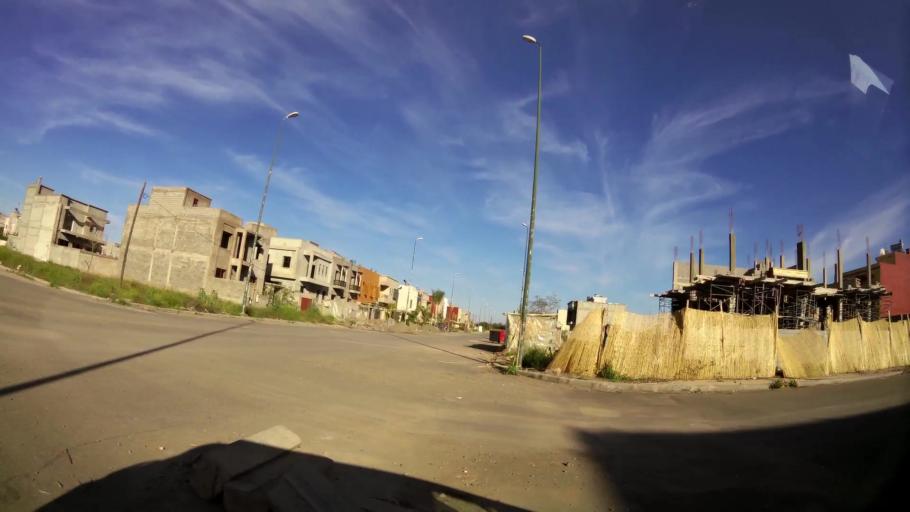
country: MA
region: Marrakech-Tensift-Al Haouz
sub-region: Marrakech
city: Marrakesh
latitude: 31.6704
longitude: -8.0716
